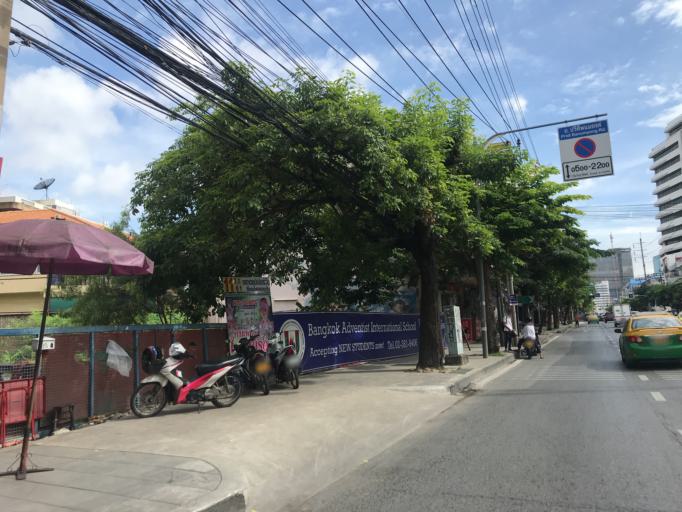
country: TH
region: Bangkok
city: Watthana
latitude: 13.7320
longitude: 100.5969
